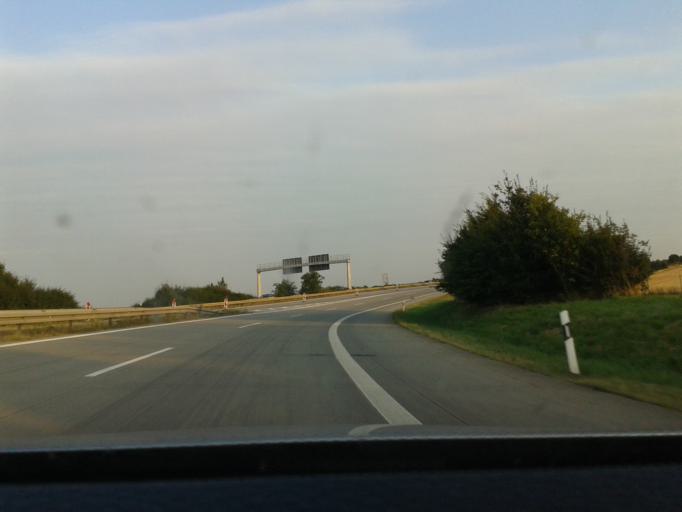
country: DE
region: Saxony
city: Wilsdruff
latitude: 51.0615
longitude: 13.6052
